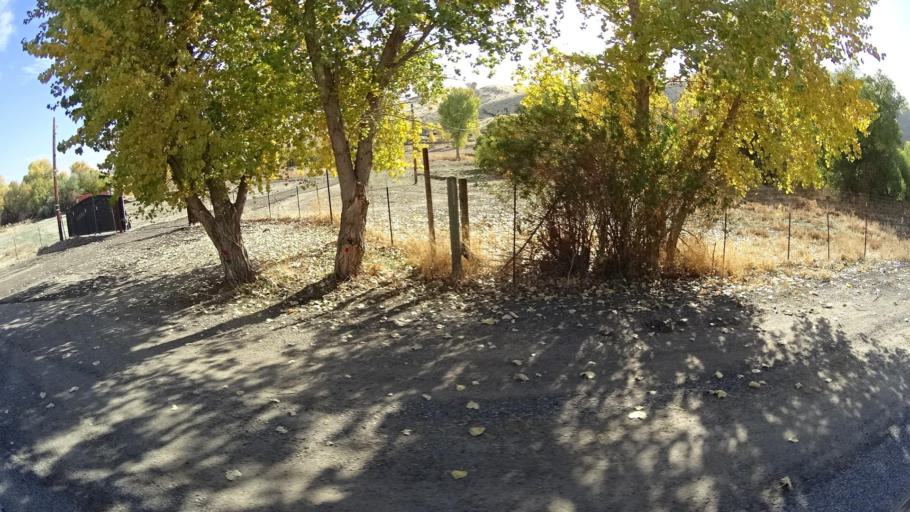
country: US
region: California
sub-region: Kern County
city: Oildale
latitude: 35.5298
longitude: -118.9554
